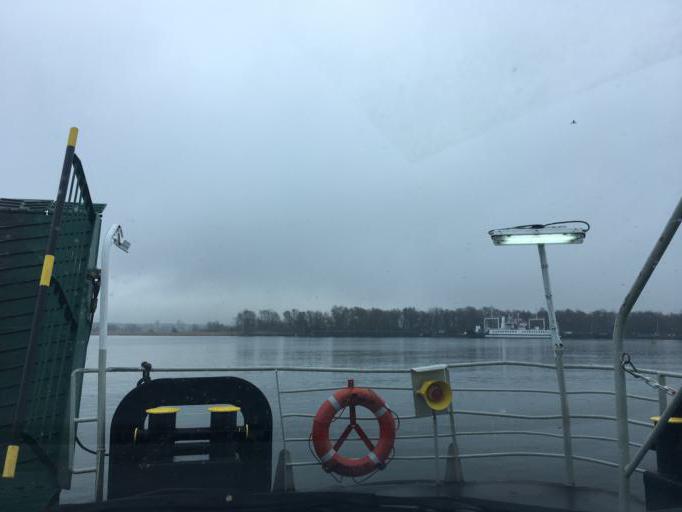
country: PL
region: West Pomeranian Voivodeship
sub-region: Swinoujscie
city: Swinoujscie
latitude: 53.8614
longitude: 14.2796
